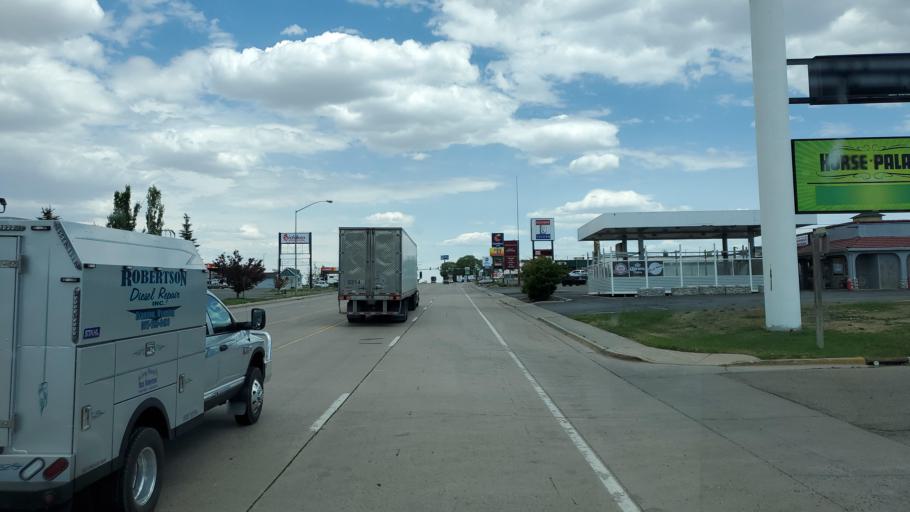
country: US
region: Wyoming
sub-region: Uinta County
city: Evanston
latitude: 41.2643
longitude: -110.9809
